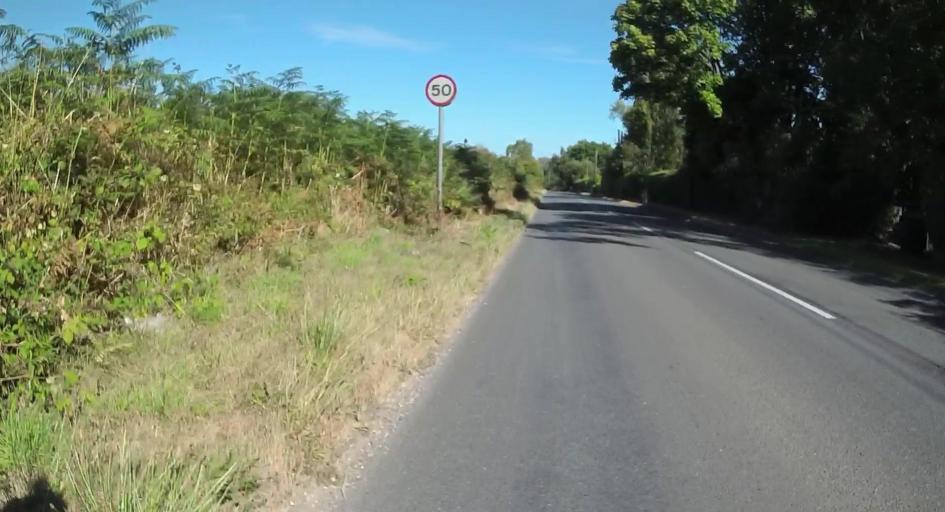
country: GB
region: England
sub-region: Dorset
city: Wareham
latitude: 50.6849
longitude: -2.1481
